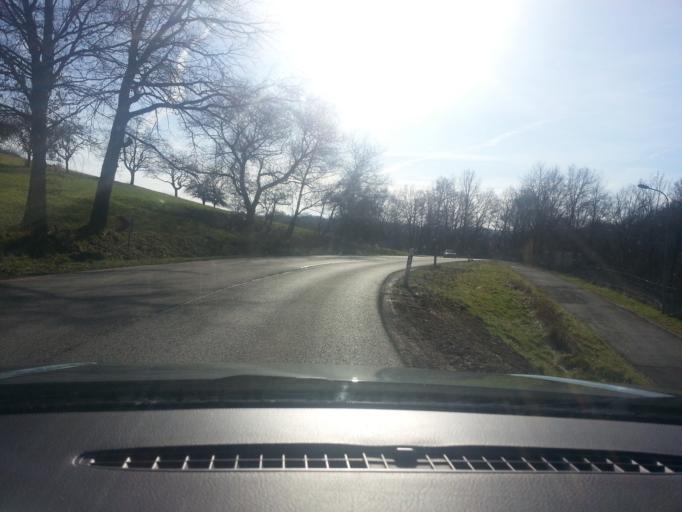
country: DE
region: Rheinland-Pfalz
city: Selchenbach
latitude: 49.4836
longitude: 7.2580
